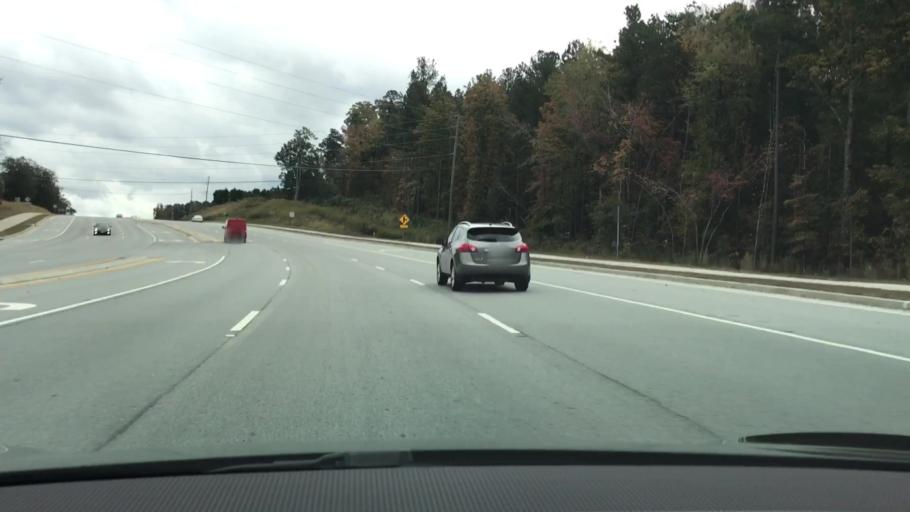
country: US
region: Georgia
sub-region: Hall County
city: Flowery Branch
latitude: 34.1199
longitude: -83.9145
